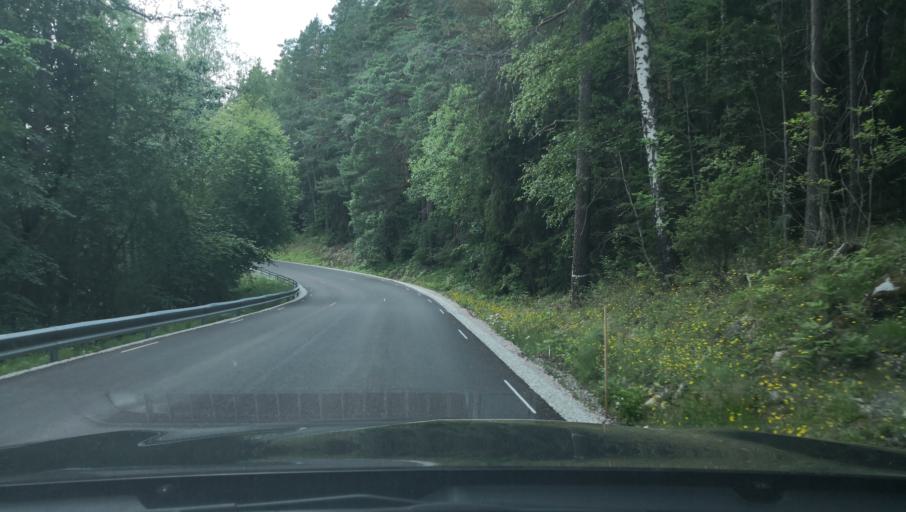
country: SE
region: Vaestmanland
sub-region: Norbergs Kommun
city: Norberg
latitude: 59.9804
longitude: 15.9133
